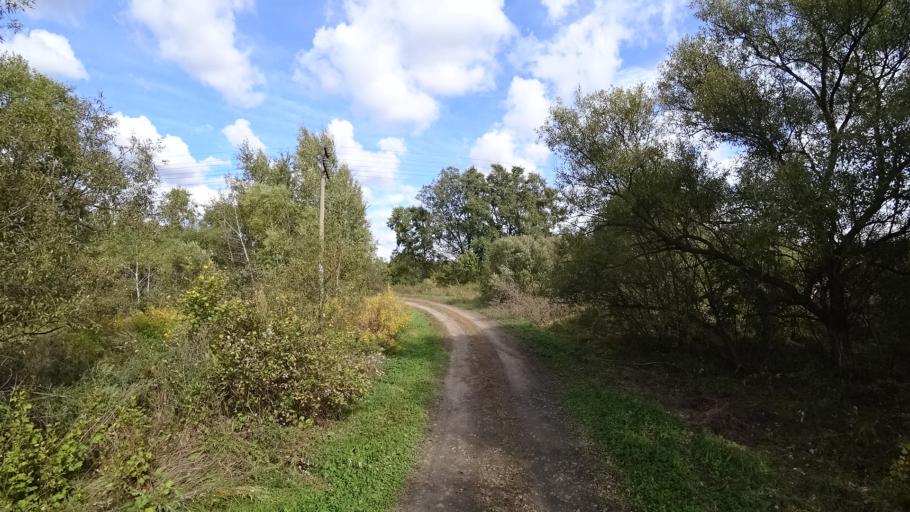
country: RU
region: Amur
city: Arkhara
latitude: 49.3436
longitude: 130.1661
